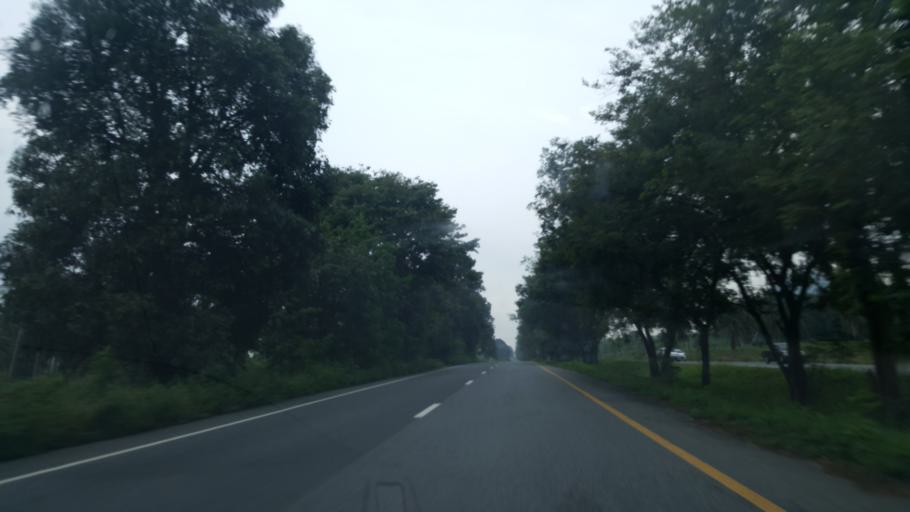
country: TH
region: Rayong
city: Ban Chang
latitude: 12.7846
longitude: 100.9920
